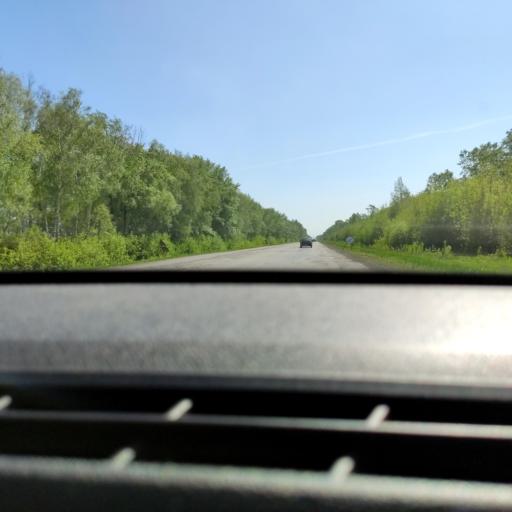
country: RU
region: Samara
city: Tol'yatti
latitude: 53.6564
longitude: 49.4245
